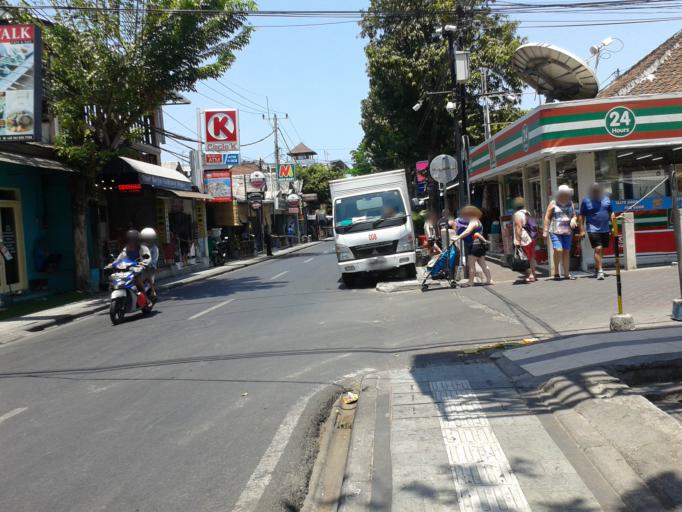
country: ID
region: Bali
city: Kuta
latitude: -8.7086
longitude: 115.1702
